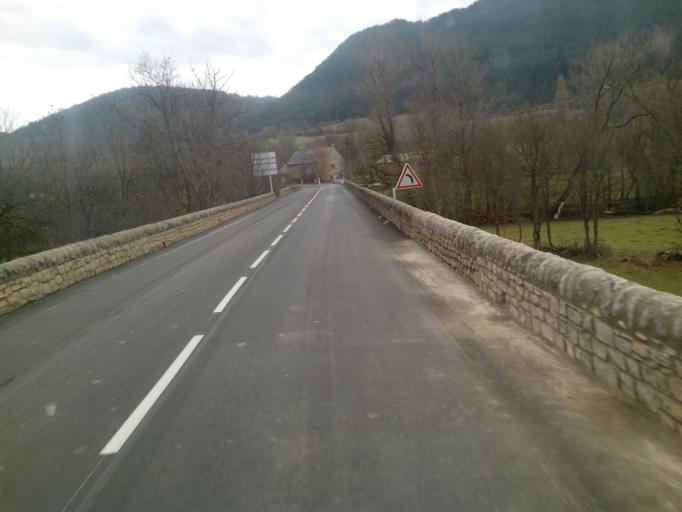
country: FR
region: Languedoc-Roussillon
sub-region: Departement de la Lozere
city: Mende
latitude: 44.4547
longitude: 3.5413
